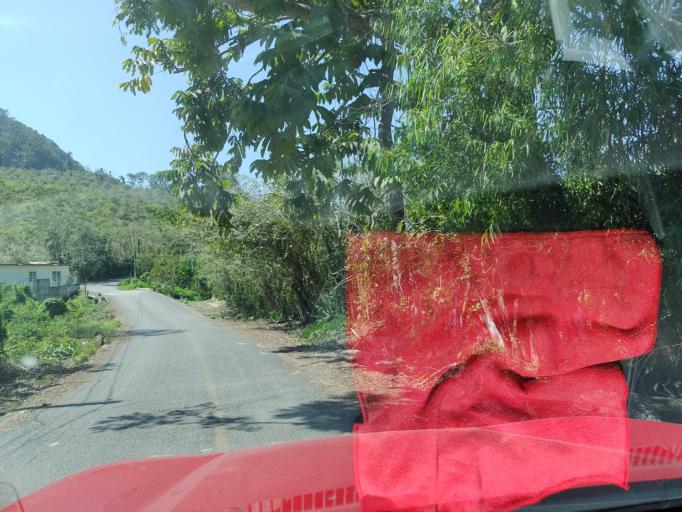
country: MX
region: Veracruz
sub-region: Papantla
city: Polutla
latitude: 20.5010
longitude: -97.2149
